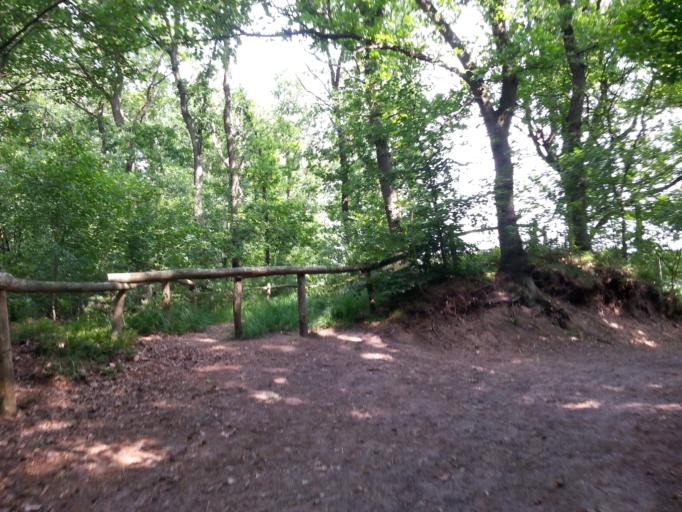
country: NL
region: Utrecht
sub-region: Gemeente Utrechtse Heuvelrug
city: Maarn
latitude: 52.0888
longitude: 5.3805
